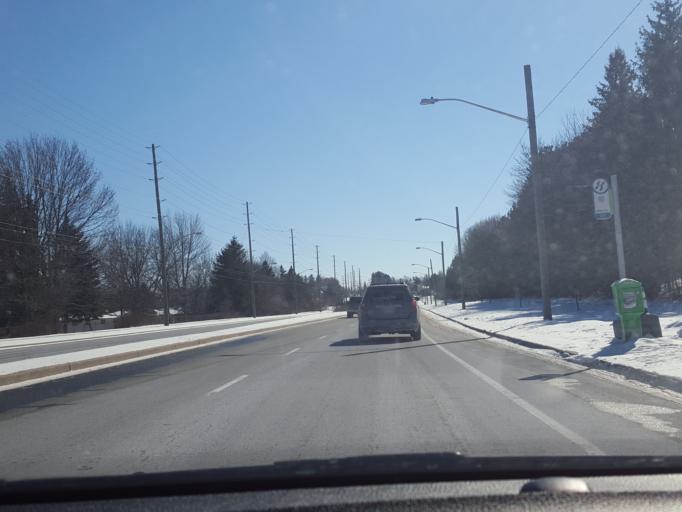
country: CA
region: Ontario
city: Waterloo
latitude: 43.4579
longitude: -80.5577
